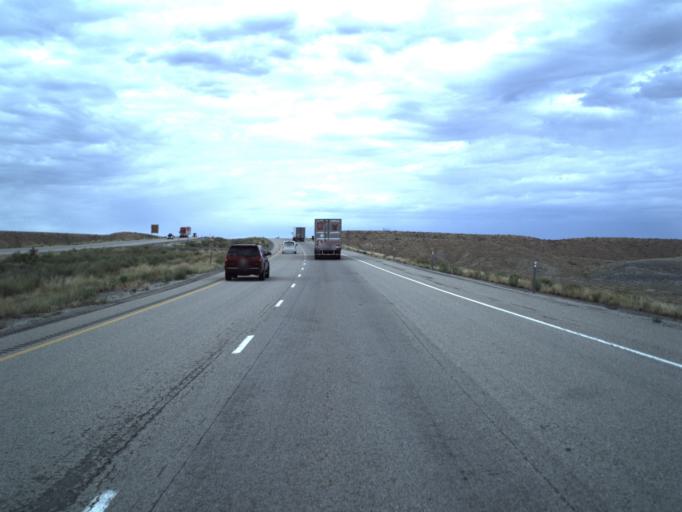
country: US
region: Utah
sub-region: Grand County
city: Moab
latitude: 38.9426
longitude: -109.4007
